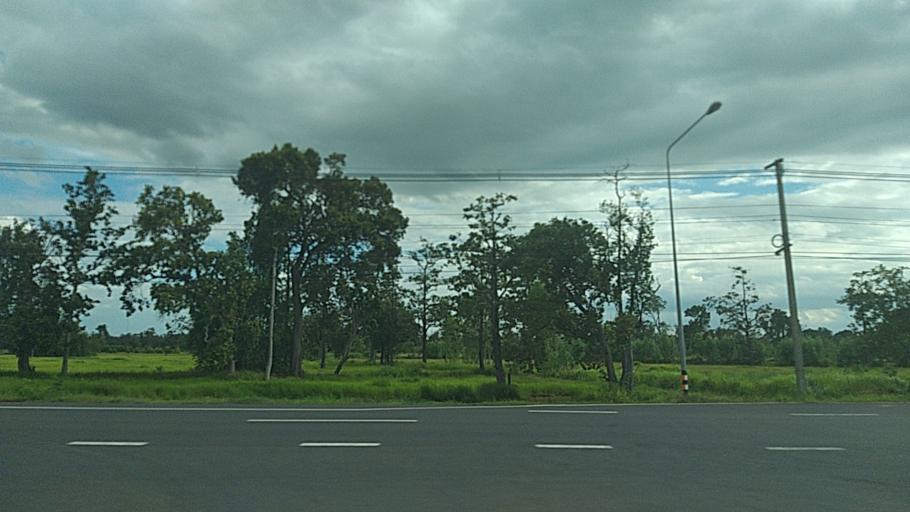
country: TH
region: Surin
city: Prasat
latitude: 14.6002
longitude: 103.4348
